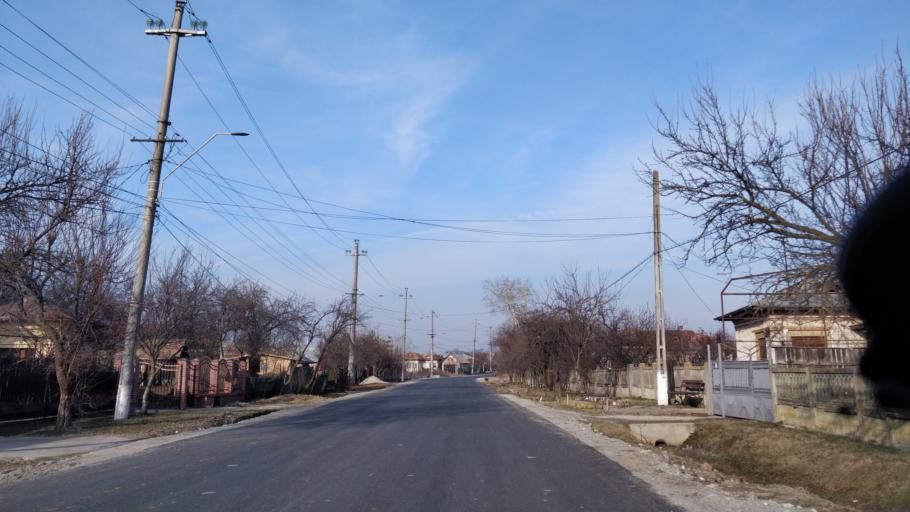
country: RO
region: Giurgiu
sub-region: Comuna Ulmi
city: Trestieni
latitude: 44.5111
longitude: 25.7643
